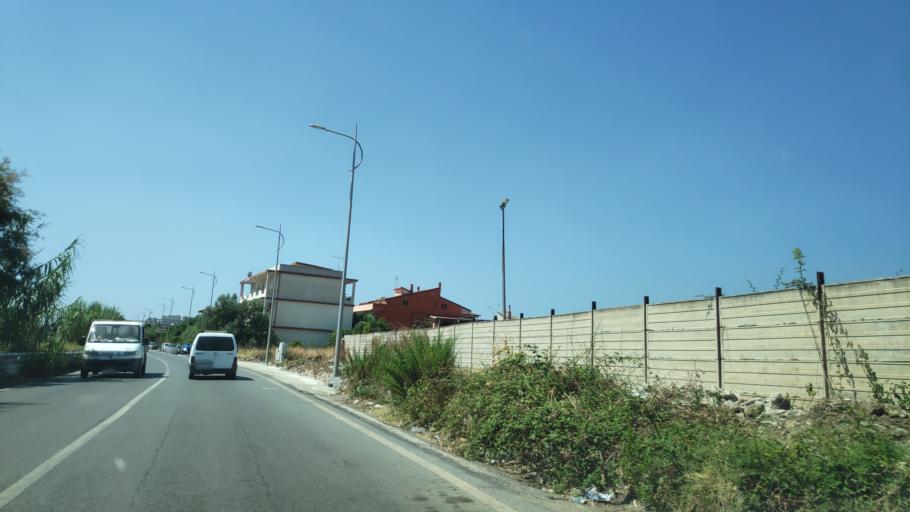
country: IT
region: Calabria
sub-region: Provincia di Reggio Calabria
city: Brancaleone-Marina
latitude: 37.9736
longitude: 16.1087
